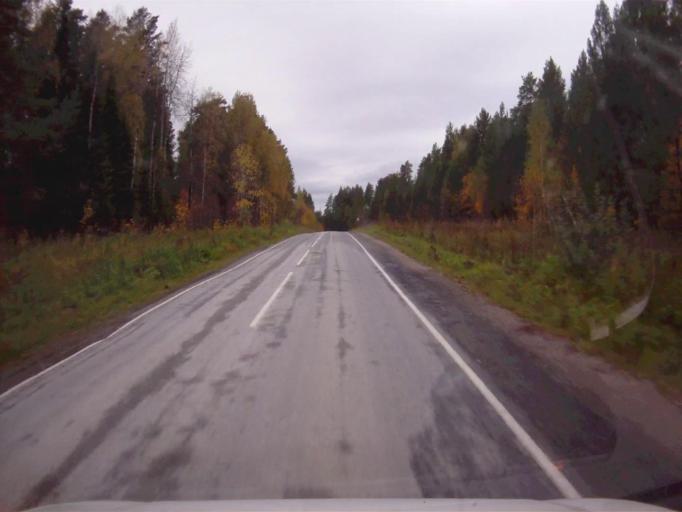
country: RU
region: Chelyabinsk
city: Nyazepetrovsk
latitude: 56.0554
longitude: 59.4744
